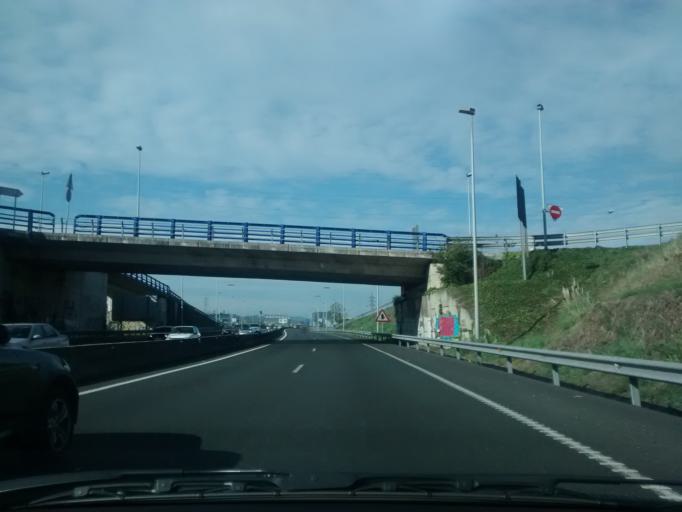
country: ES
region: Cantabria
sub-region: Provincia de Cantabria
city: El Astillero
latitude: 43.4053
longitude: -3.8229
